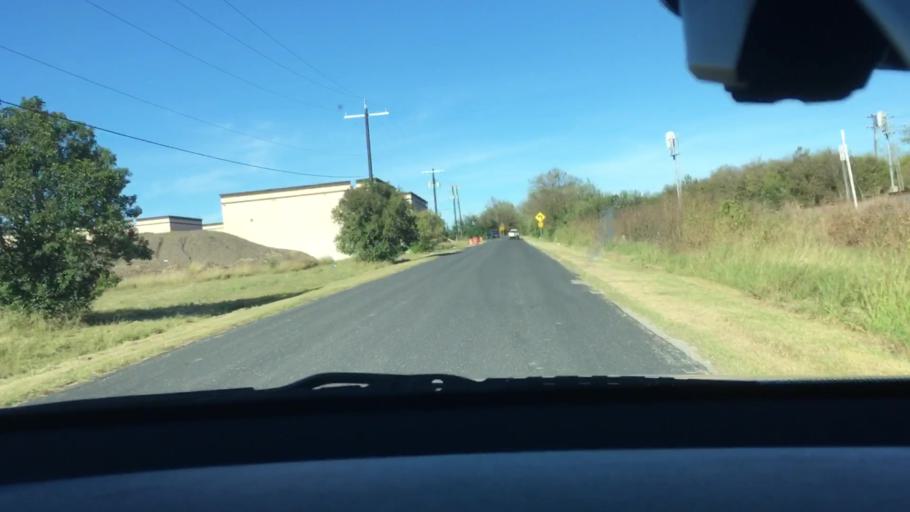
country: US
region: Texas
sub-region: Bexar County
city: Converse
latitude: 29.5245
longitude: -98.3094
